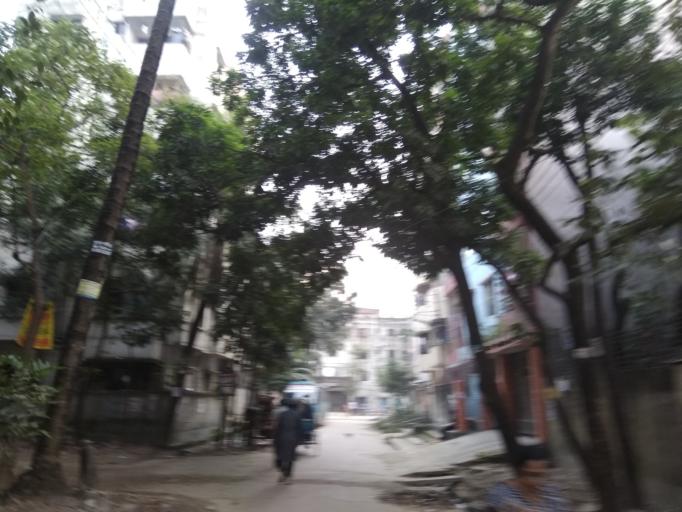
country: BD
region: Dhaka
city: Tungi
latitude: 23.8142
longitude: 90.3643
